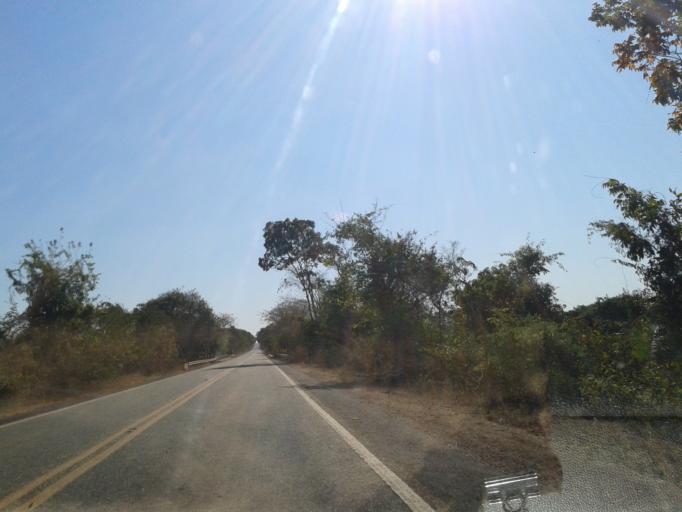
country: BR
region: Goias
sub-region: Mozarlandia
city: Mozarlandia
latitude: -14.4905
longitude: -50.4820
